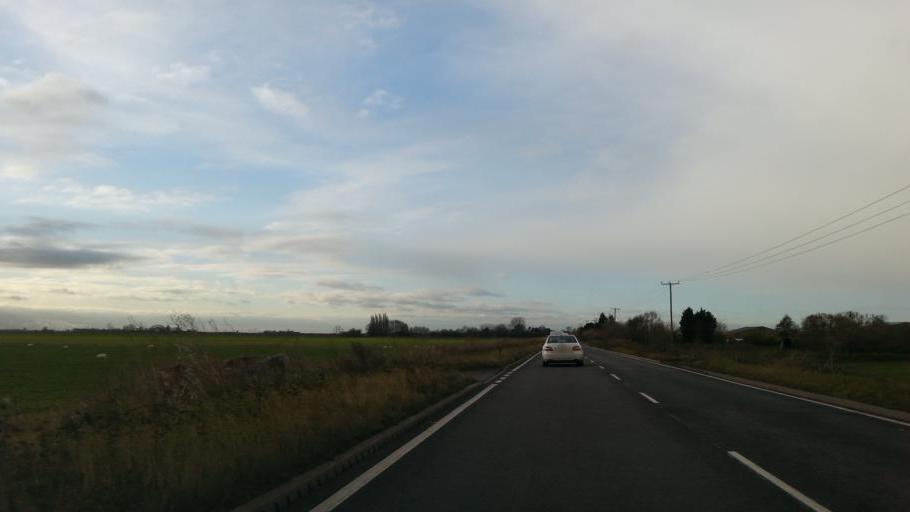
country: GB
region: England
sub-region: Cambridgeshire
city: March
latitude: 52.6111
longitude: 0.0269
